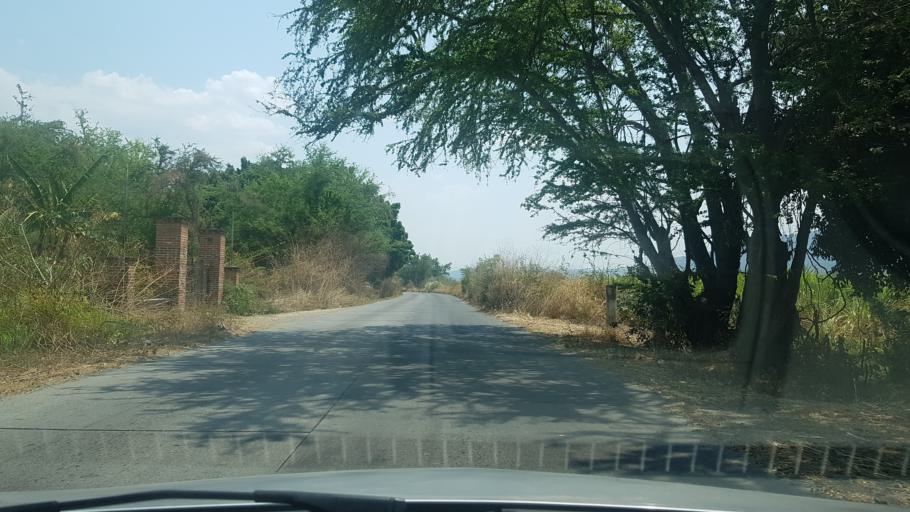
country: MX
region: Morelos
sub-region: Jiutepec
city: Independencia
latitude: 18.7919
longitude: -99.1036
